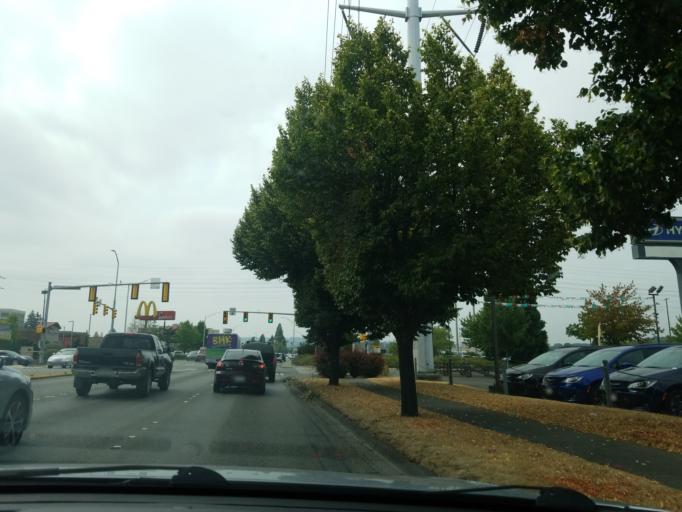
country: US
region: Washington
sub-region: King County
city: Renton
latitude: 47.4719
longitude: -122.2117
